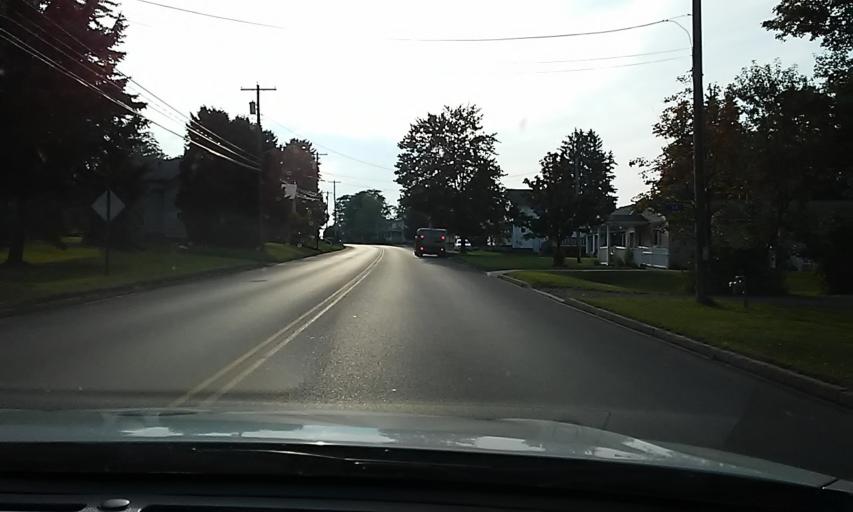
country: US
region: Pennsylvania
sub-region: McKean County
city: Kane
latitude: 41.7256
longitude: -78.6318
